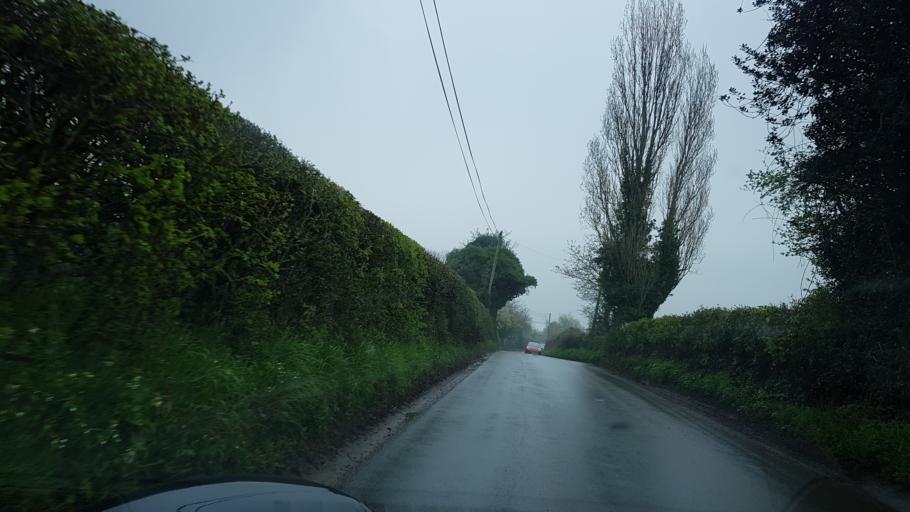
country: GB
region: England
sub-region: Herefordshire
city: Sellack
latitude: 51.9615
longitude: -2.6513
